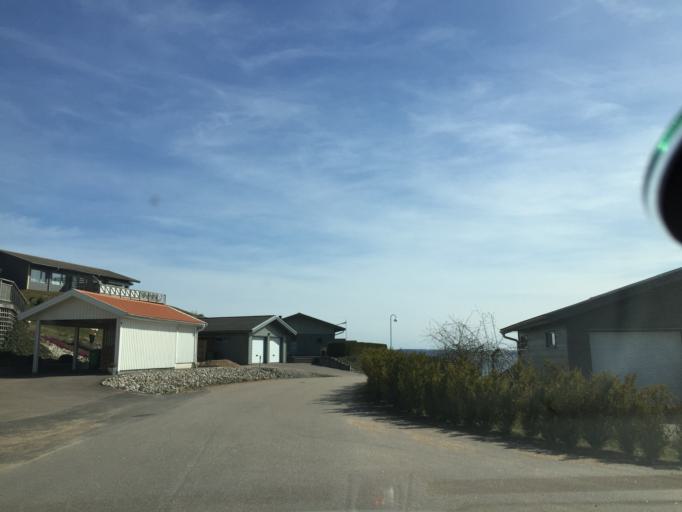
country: SE
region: Vaestra Goetaland
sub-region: Orust
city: Henan
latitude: 58.3437
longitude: 11.7317
